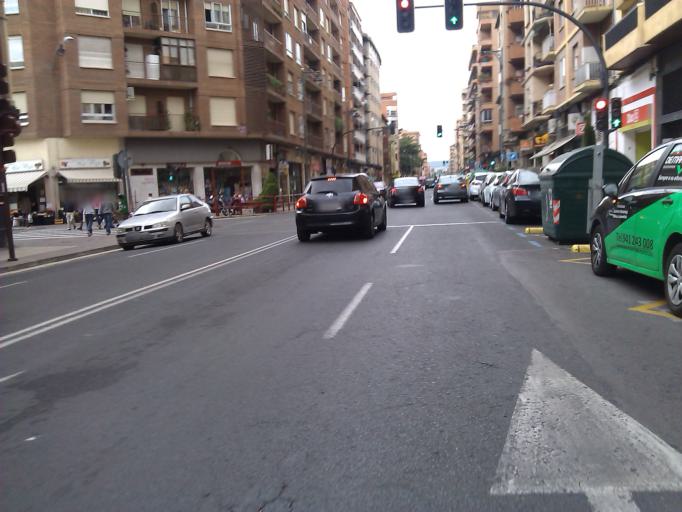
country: ES
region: La Rioja
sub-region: Provincia de La Rioja
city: Logrono
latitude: 42.4654
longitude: -2.4550
